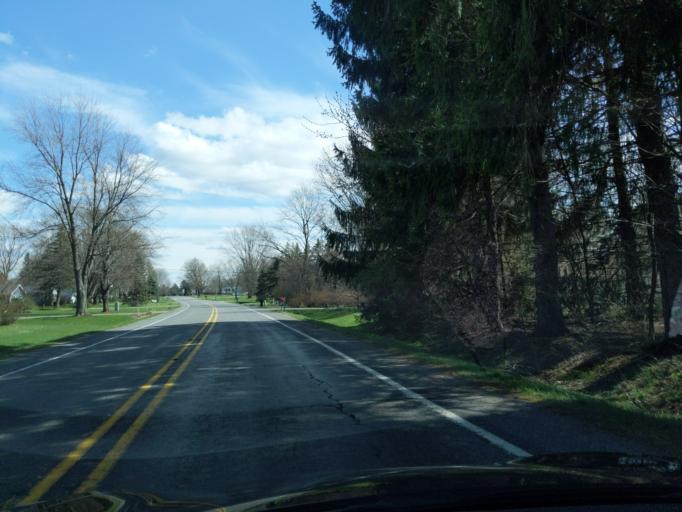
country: US
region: Michigan
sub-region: Ingham County
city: Mason
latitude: 42.5600
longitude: -84.4077
